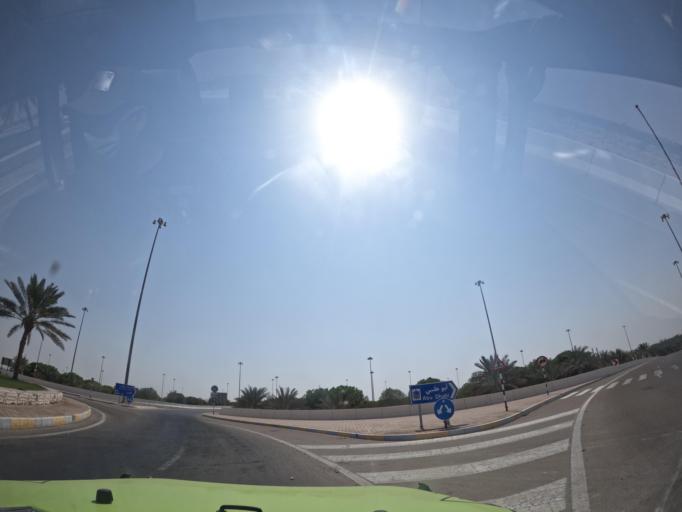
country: AE
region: Abu Dhabi
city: Al Ain
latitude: 24.1768
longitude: 55.1334
